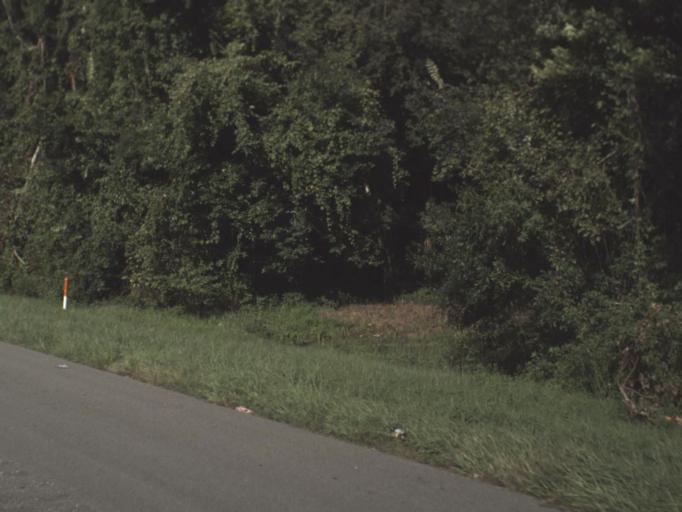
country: US
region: Florida
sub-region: Hillsborough County
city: Pebble Creek
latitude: 28.1649
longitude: -82.3991
